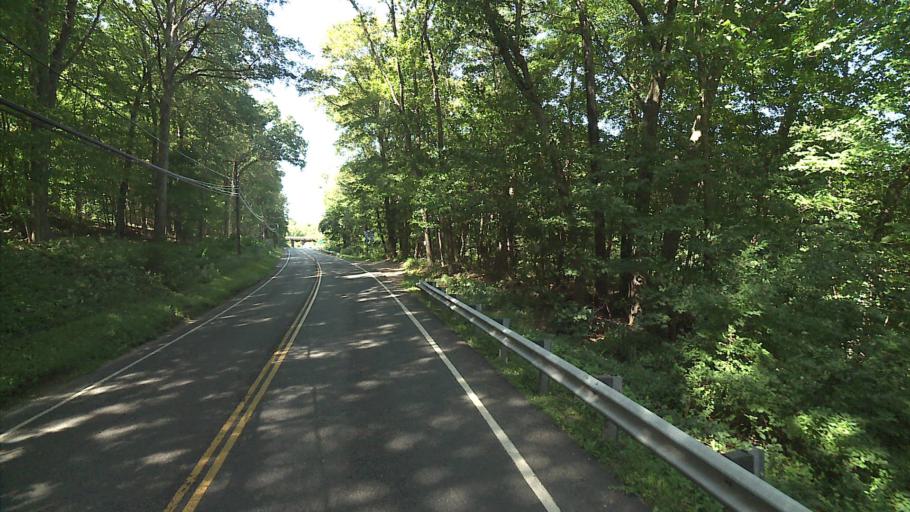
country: US
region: Connecticut
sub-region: New Haven County
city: Middlebury
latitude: 41.4916
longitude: -73.1599
